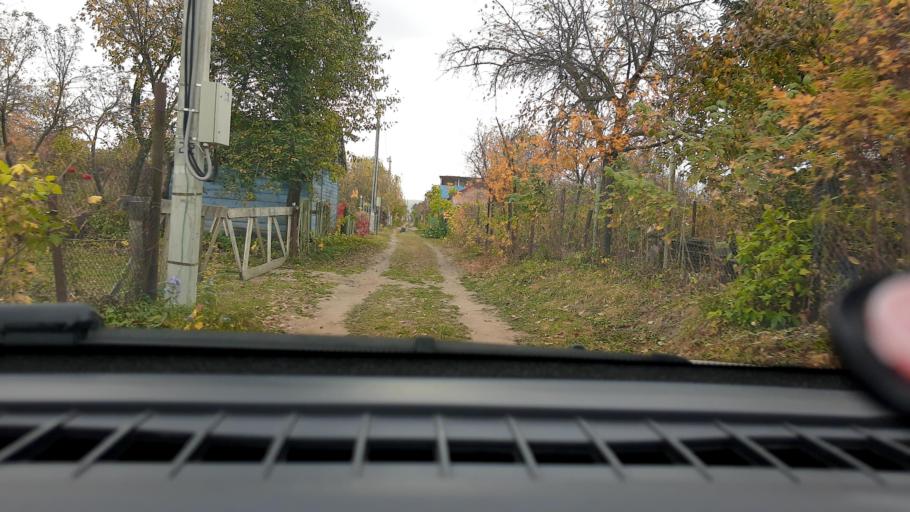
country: RU
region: Nizjnij Novgorod
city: Nizhniy Novgorod
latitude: 56.2696
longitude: 43.9573
